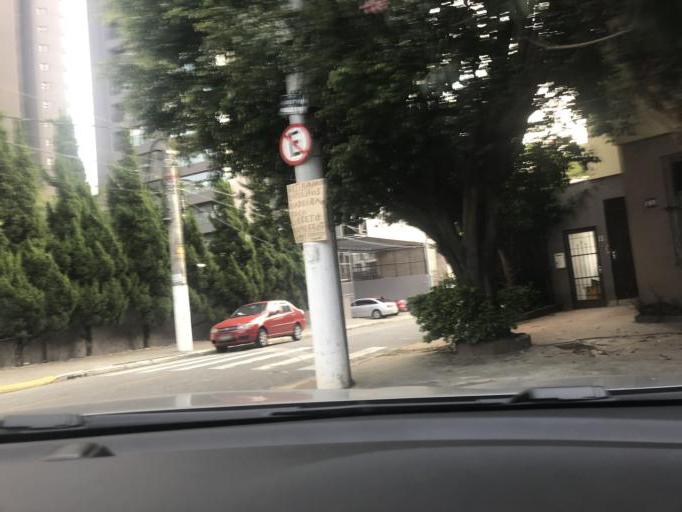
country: BR
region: Sao Paulo
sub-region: Osasco
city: Osasco
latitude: -23.5540
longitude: -46.7631
